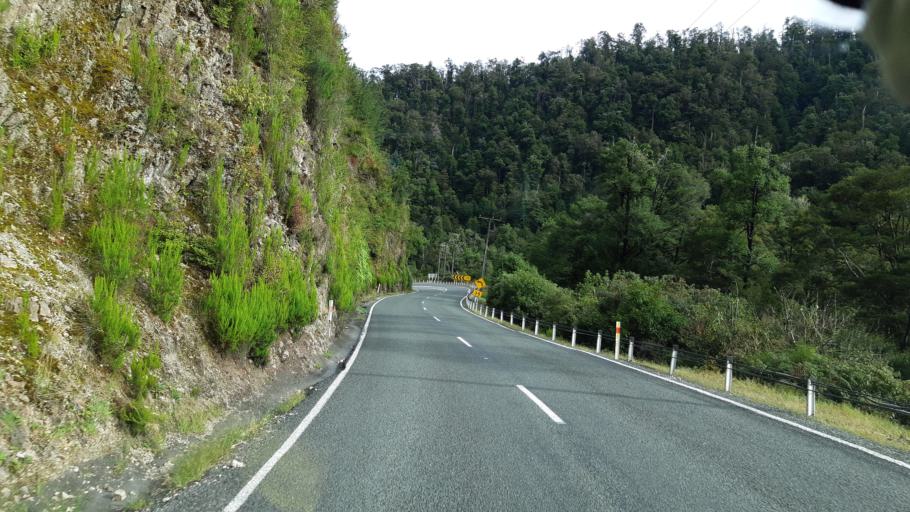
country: NZ
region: West Coast
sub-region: Buller District
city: Westport
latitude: -41.9893
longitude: 172.2185
